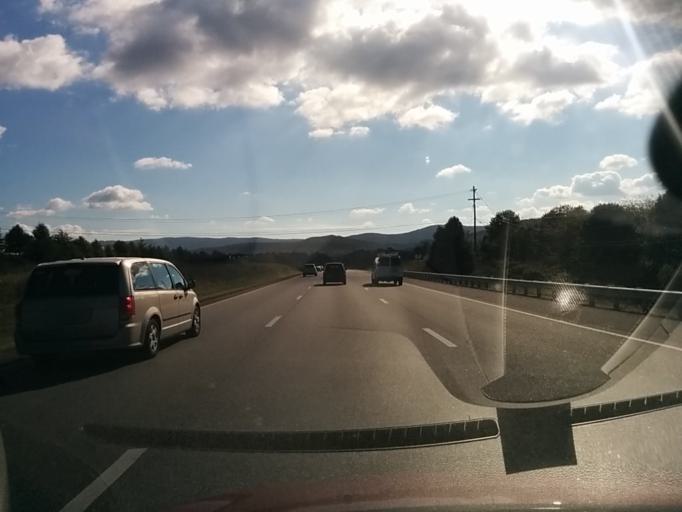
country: US
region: Virginia
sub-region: Augusta County
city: Lyndhurst
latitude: 38.0594
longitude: -78.9364
